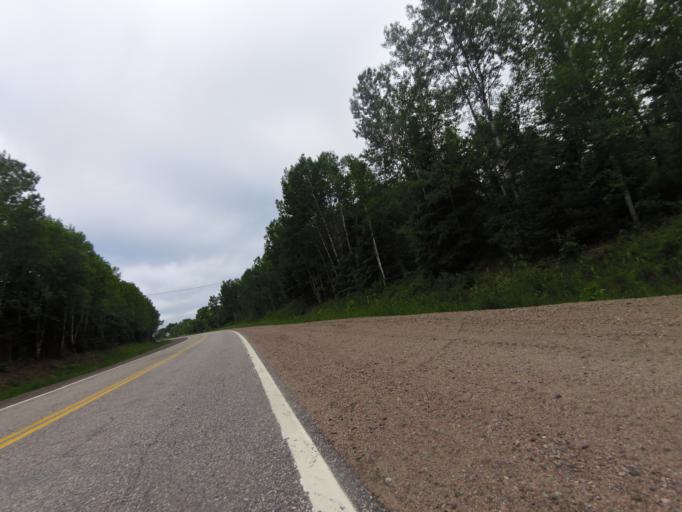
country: CA
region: Quebec
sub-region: Outaouais
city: Shawville
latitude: 45.9116
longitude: -76.3158
